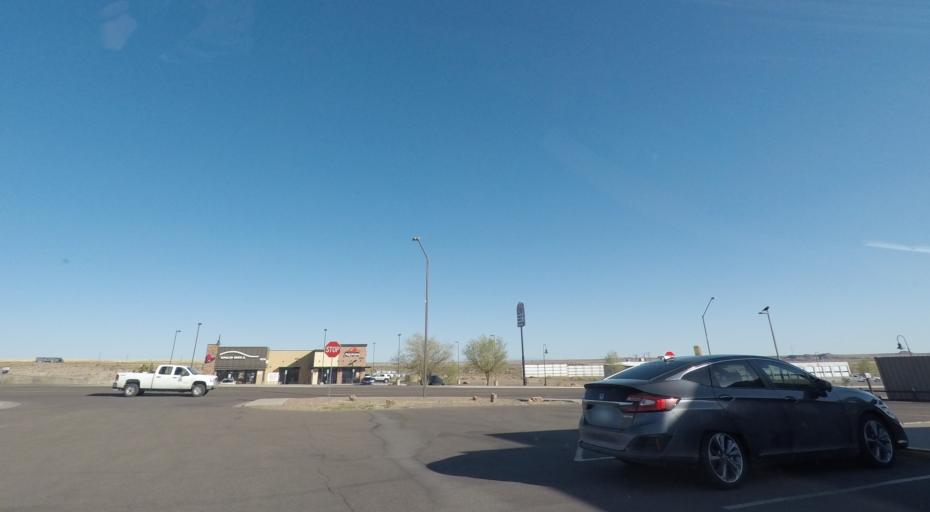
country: US
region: Arizona
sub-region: Navajo County
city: Holbrook
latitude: 34.9191
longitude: -110.1512
